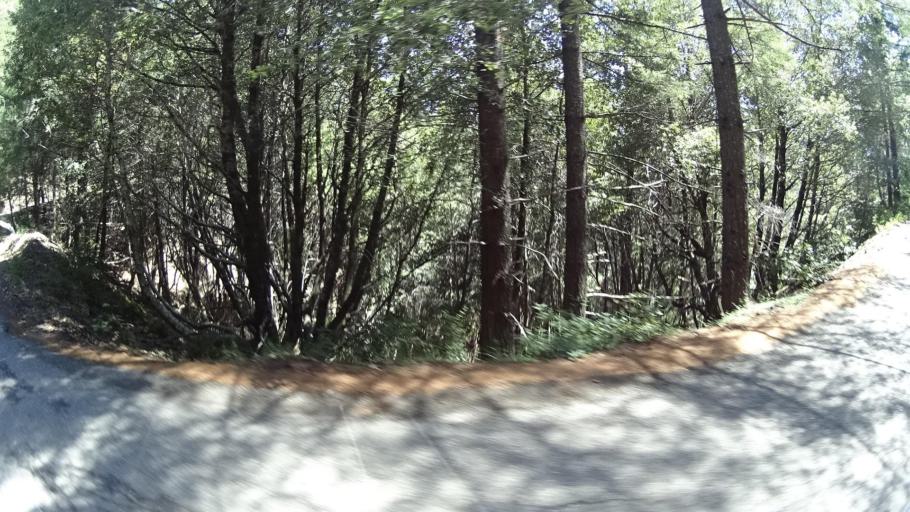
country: US
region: California
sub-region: Humboldt County
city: Rio Dell
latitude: 40.2688
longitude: -124.0826
